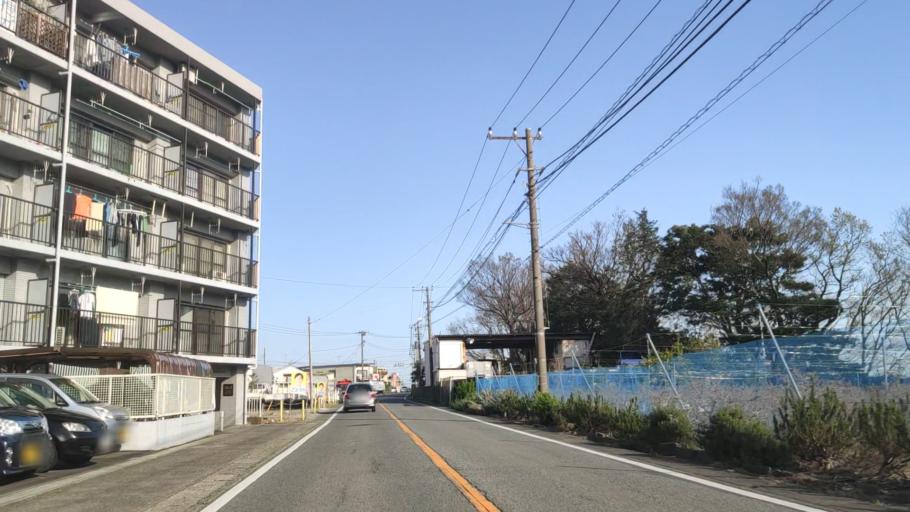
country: JP
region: Kanagawa
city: Zama
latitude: 35.5054
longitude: 139.3476
